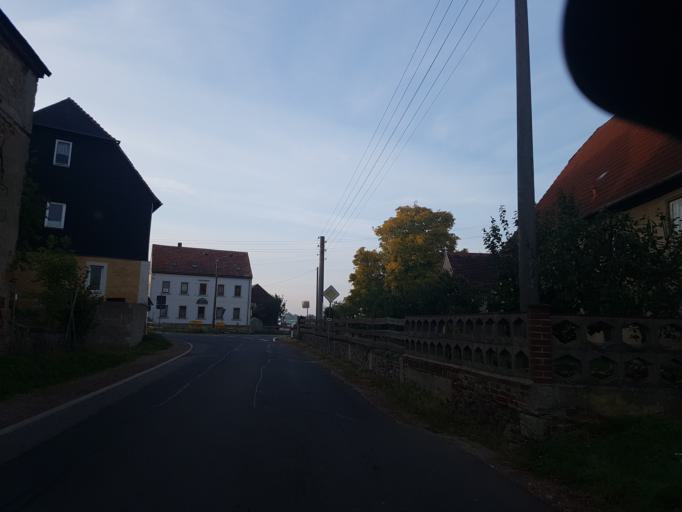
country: DE
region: Saxony
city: Waldheim
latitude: 51.1021
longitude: 13.0570
